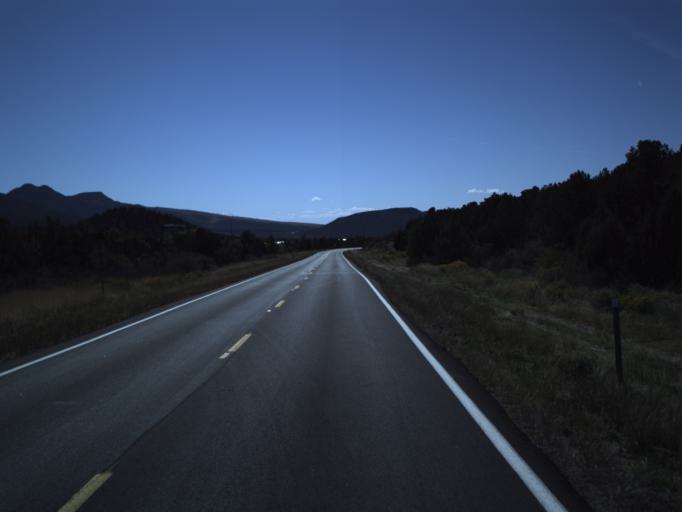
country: US
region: Utah
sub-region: Washington County
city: Enterprise
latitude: 37.4304
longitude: -113.6292
